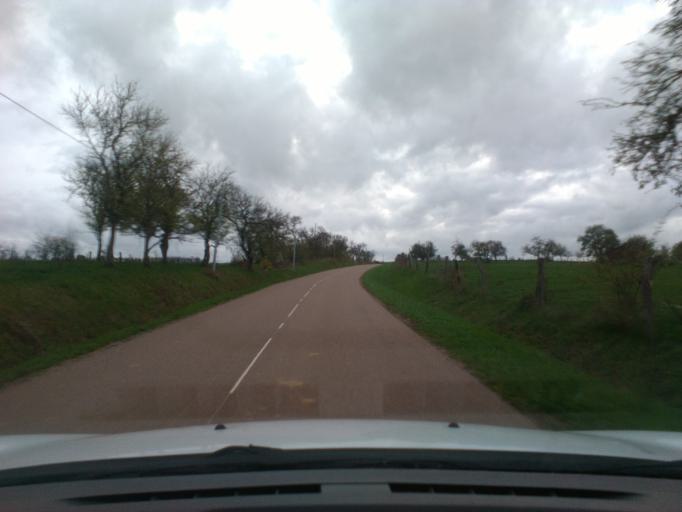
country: FR
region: Lorraine
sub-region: Departement des Vosges
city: Mirecourt
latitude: 48.3541
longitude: 6.0812
